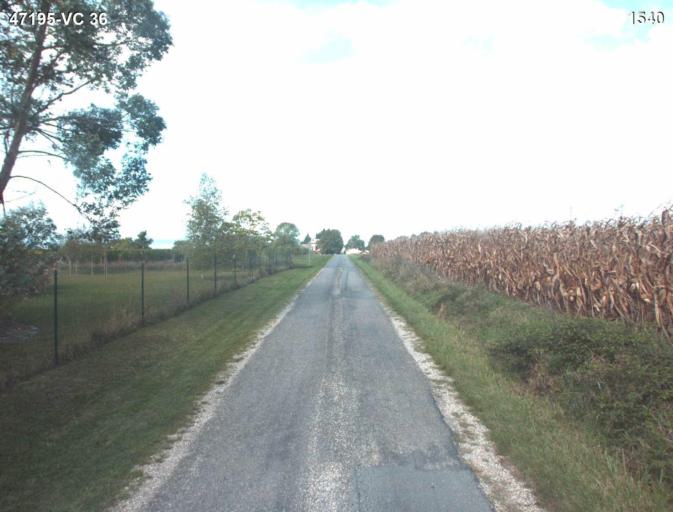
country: FR
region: Aquitaine
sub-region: Departement du Lot-et-Garonne
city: Nerac
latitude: 44.1226
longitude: 0.3302
